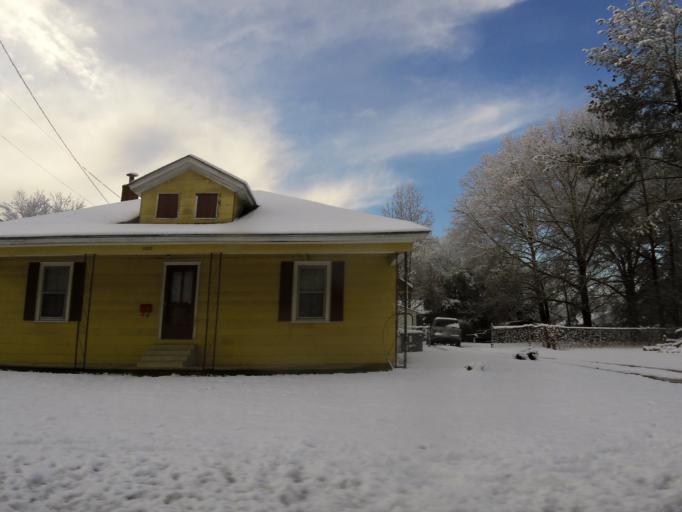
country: US
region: North Carolina
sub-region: Nash County
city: Rocky Mount
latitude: 35.9302
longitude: -77.8193
